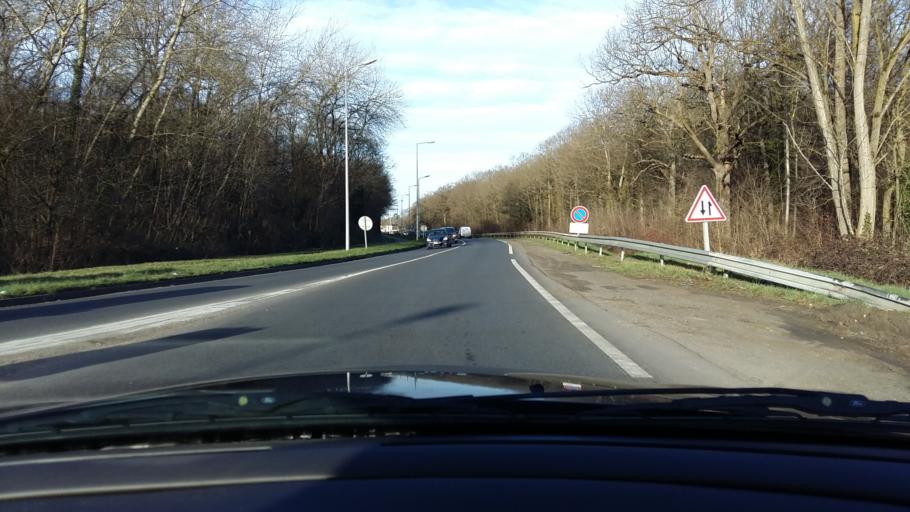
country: FR
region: Ile-de-France
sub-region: Departement de l'Essonne
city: Fleury-Merogis
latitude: 48.6352
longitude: 2.3585
